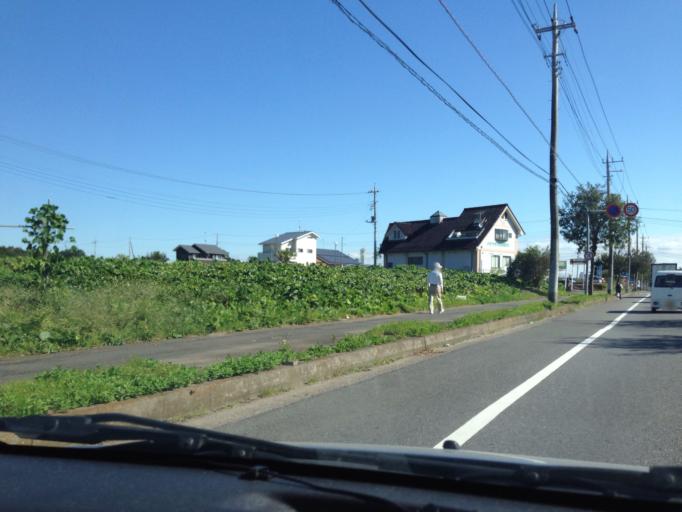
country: JP
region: Ibaraki
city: Ami
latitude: 36.0405
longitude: 140.2040
